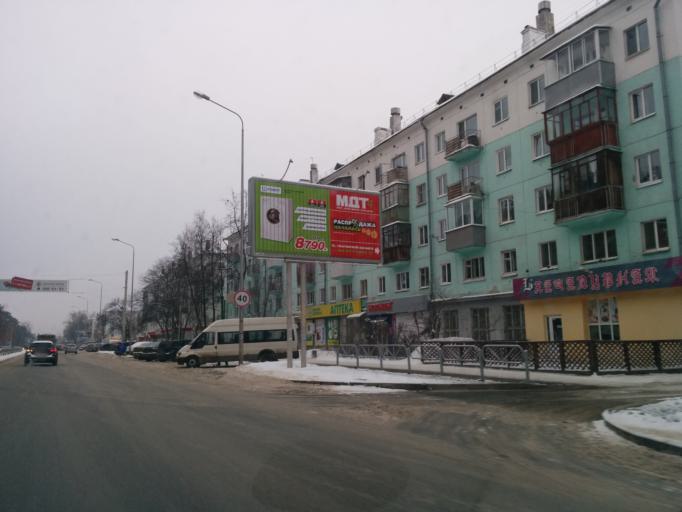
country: RU
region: Perm
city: Kultayevo
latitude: 58.0158
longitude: 55.9803
